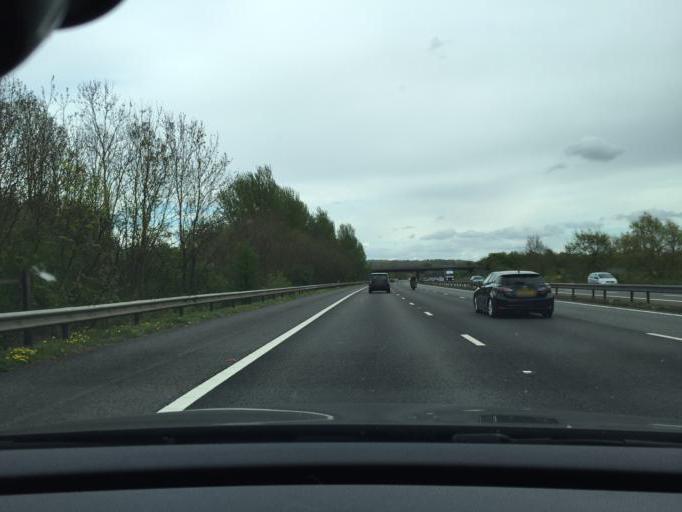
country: GB
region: England
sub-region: West Berkshire
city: Pangbourne
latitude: 51.4586
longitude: -1.0949
